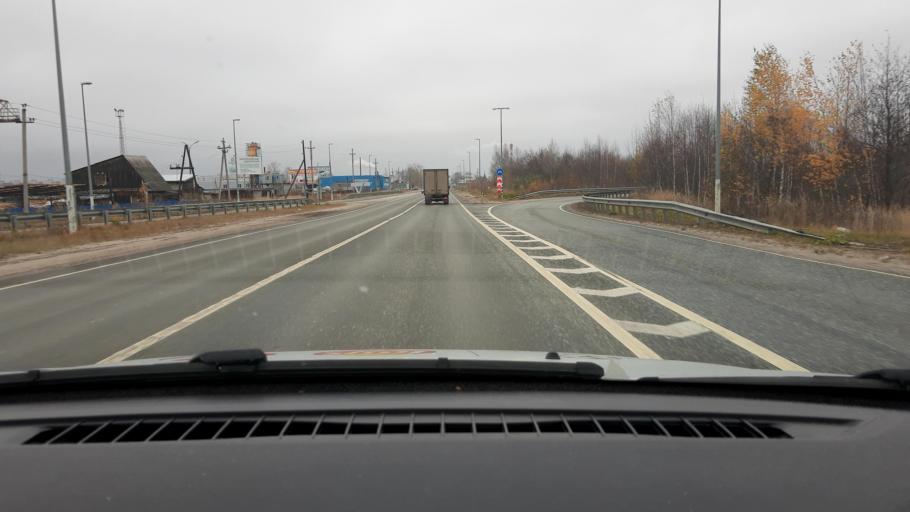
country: RU
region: Nizjnij Novgorod
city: Zavolzh'ye
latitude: 56.6192
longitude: 43.4310
